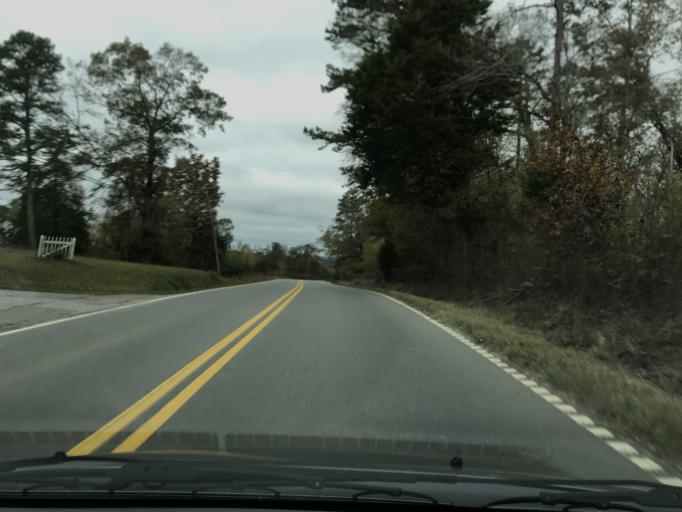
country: US
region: Tennessee
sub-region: Hamilton County
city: Sale Creek
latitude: 35.3694
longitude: -84.9932
